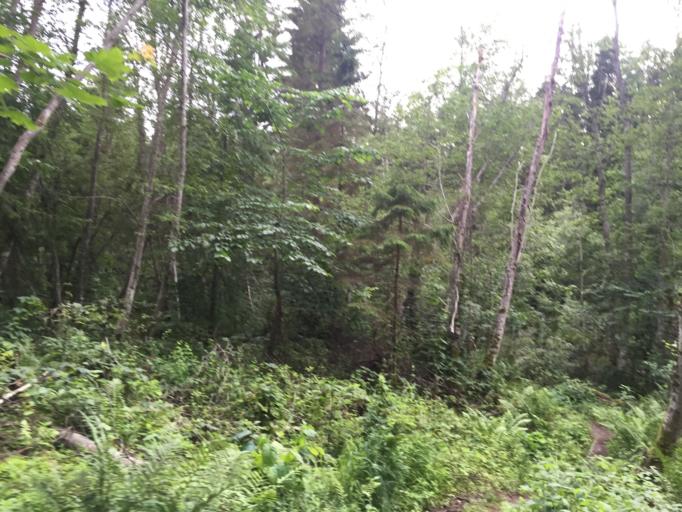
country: LV
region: Ligatne
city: Ligatne
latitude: 57.2336
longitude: 25.1516
